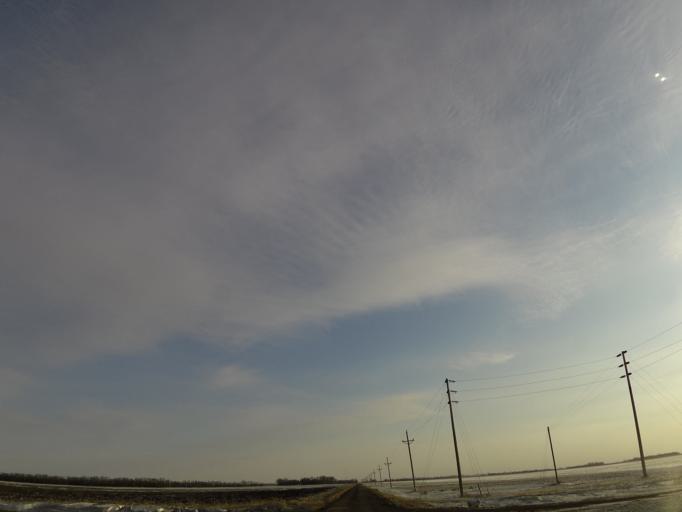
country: US
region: North Dakota
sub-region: Walsh County
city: Grafton
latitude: 48.3983
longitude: -97.4267
